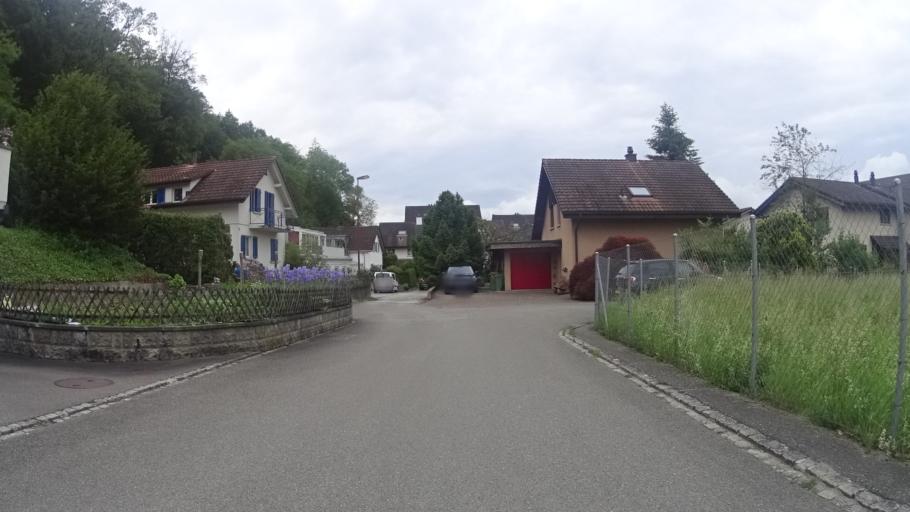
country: CH
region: Aargau
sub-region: Bezirk Brugg
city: Lauffohr (Brugg)
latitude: 47.5175
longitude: 8.2424
